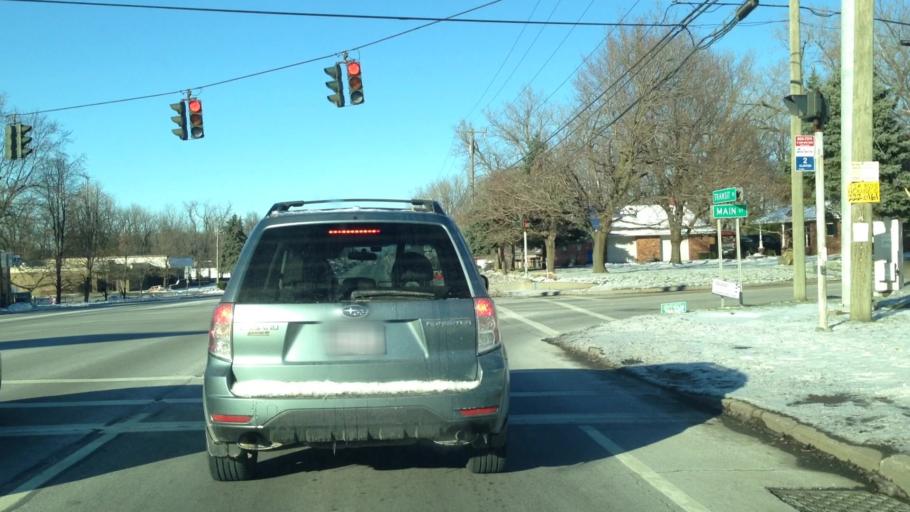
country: US
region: New York
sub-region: Erie County
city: Depew
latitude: 42.8554
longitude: -78.6968
